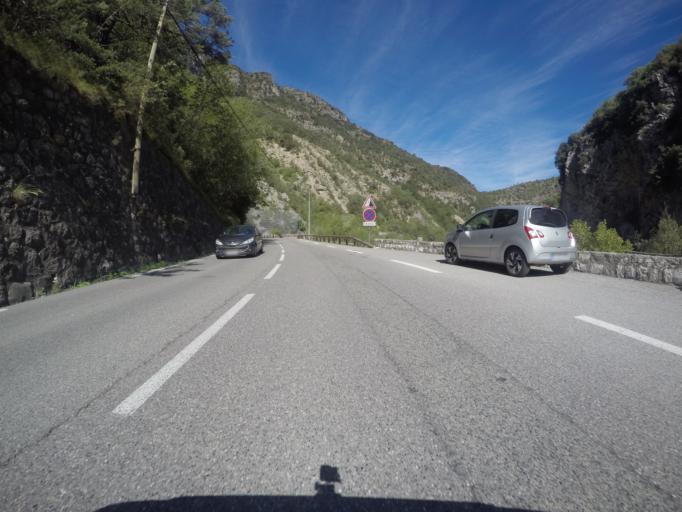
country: FR
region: Provence-Alpes-Cote d'Azur
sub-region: Departement des Alpes-Maritimes
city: Gilette
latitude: 43.9315
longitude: 7.1758
